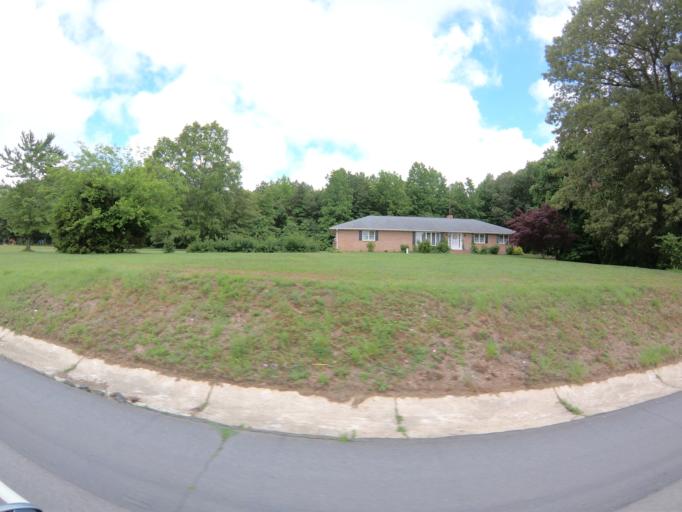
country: US
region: Maryland
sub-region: Caroline County
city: Greensboro
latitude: 39.0313
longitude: -75.7346
